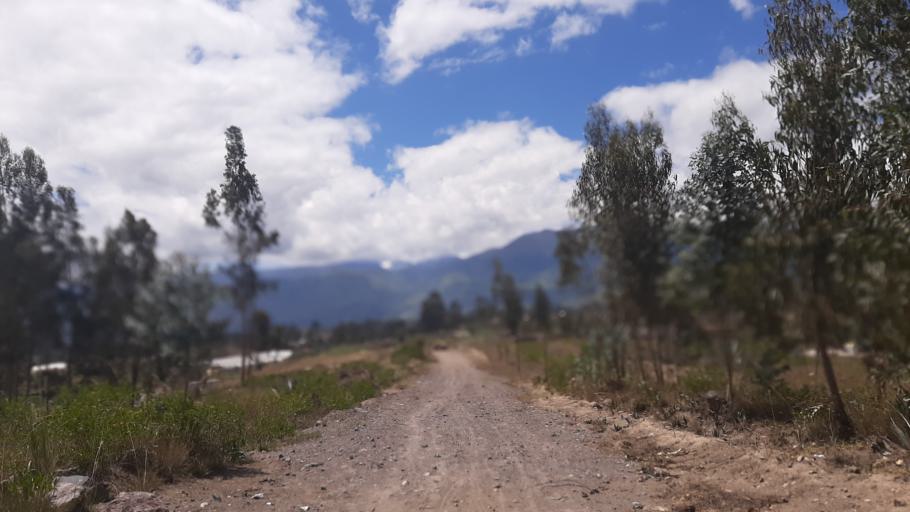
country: EC
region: Chimborazo
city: Riobamba
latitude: -1.6510
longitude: -78.6348
